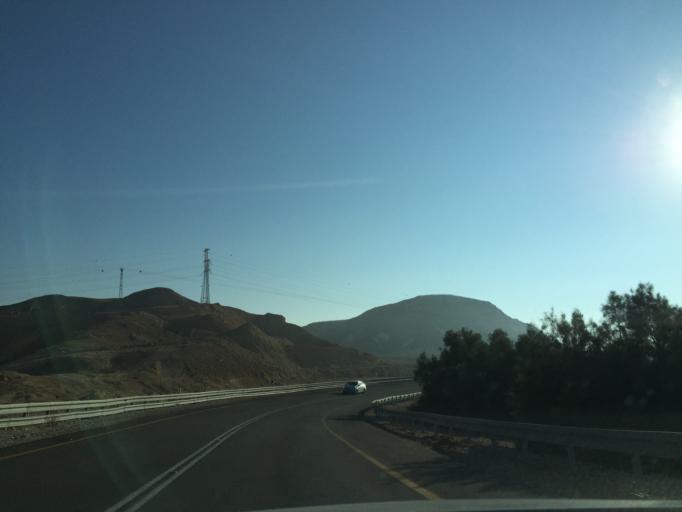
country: IL
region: Southern District
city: Mitzpe Ramon
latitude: 30.3204
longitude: 34.9655
